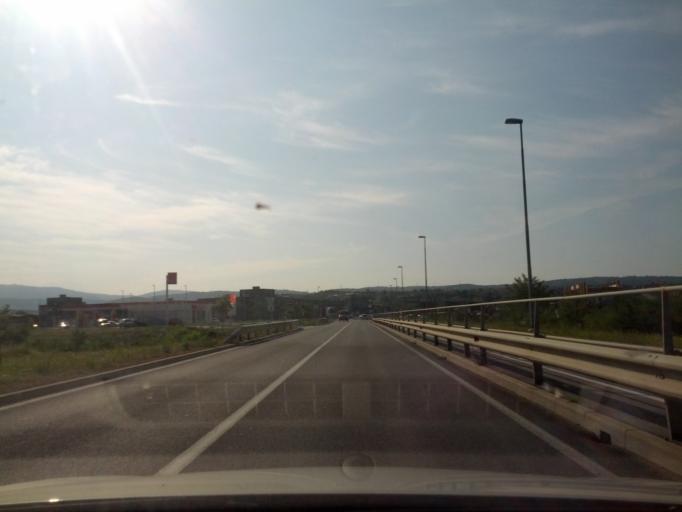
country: SI
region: Koper-Capodistria
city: Prade
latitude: 45.5521
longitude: 13.7584
